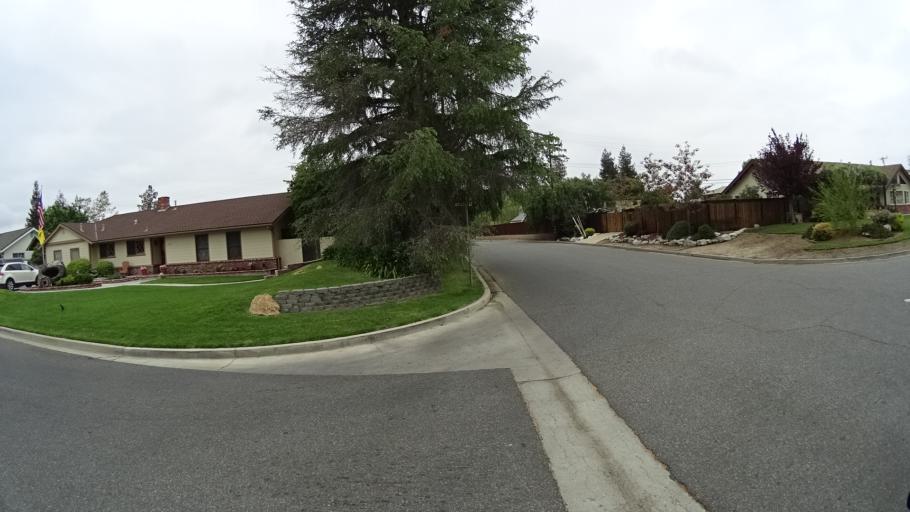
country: US
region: California
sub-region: Ventura County
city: Thousand Oaks
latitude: 34.2020
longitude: -118.8653
